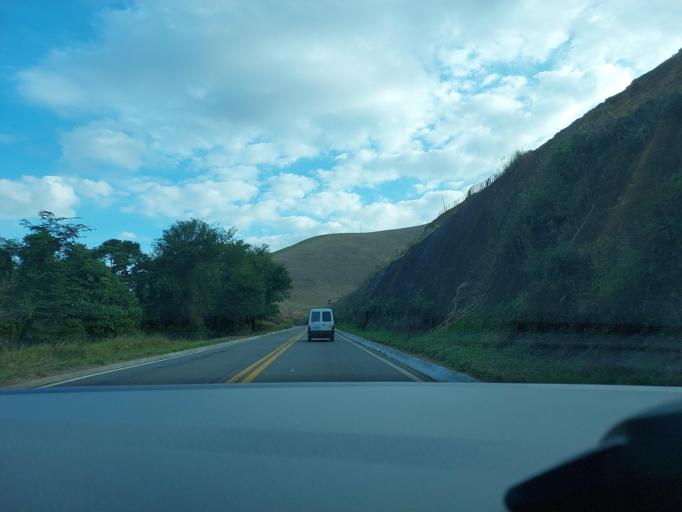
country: BR
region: Minas Gerais
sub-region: Muriae
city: Muriae
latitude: -21.0598
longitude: -42.5014
